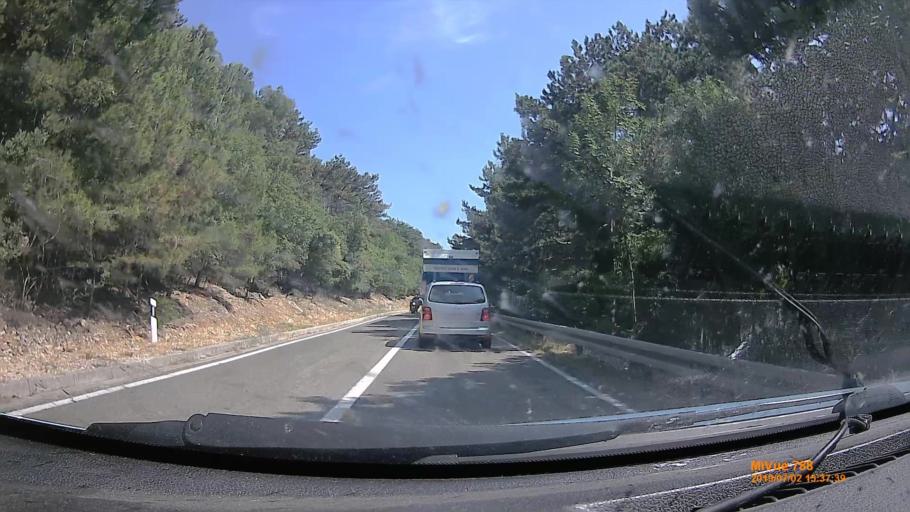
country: HR
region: Primorsko-Goranska
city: Cres
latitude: 44.9779
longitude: 14.4166
